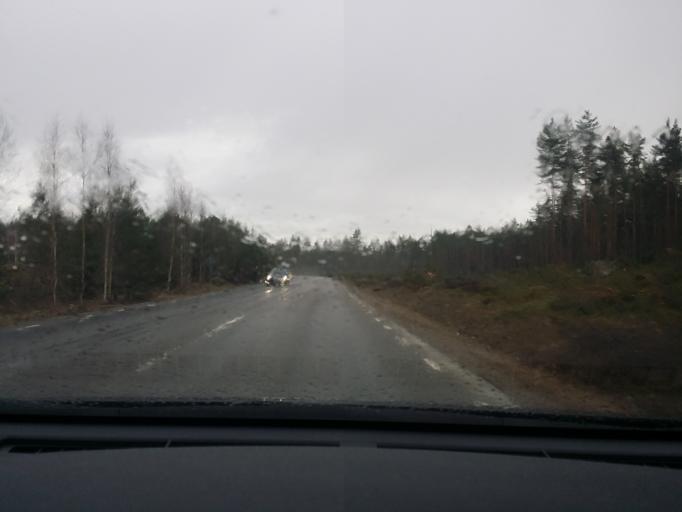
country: SE
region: Soedermanland
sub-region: Eskilstuna Kommun
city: Arla
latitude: 59.3643
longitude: 16.6817
